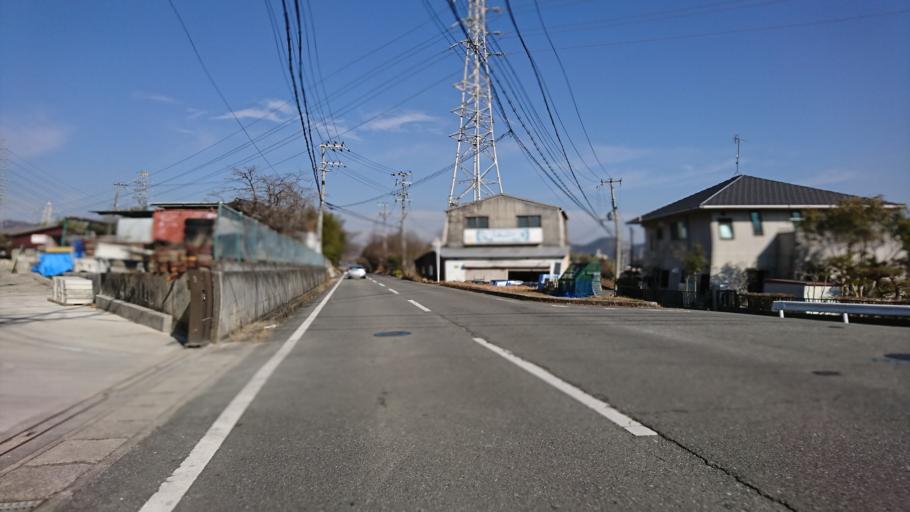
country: JP
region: Hyogo
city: Kakogawacho-honmachi
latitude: 34.7993
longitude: 134.8576
